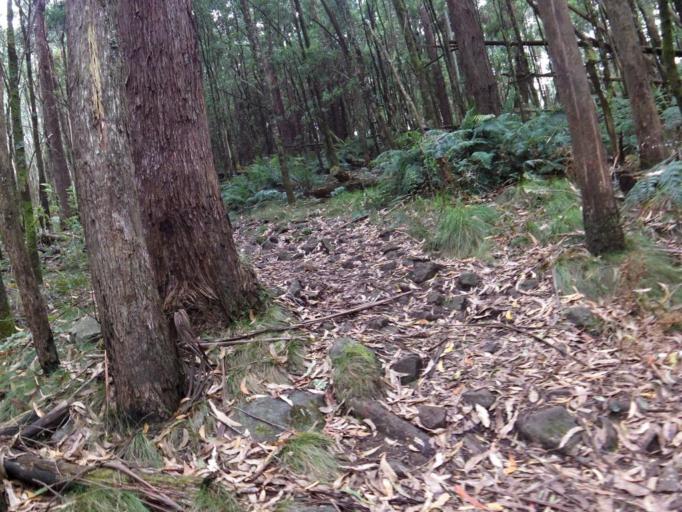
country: AU
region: Victoria
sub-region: Hume
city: Sunbury
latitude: -37.3914
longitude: 144.5772
